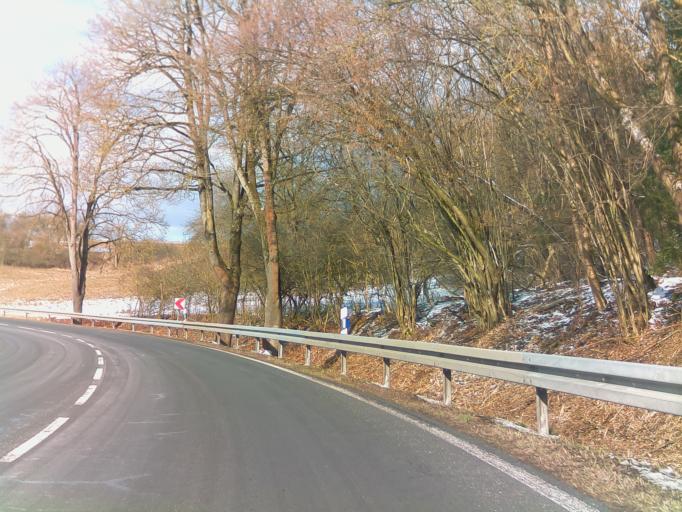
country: DE
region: Thuringia
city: Rohr
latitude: 50.6037
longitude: 10.5111
